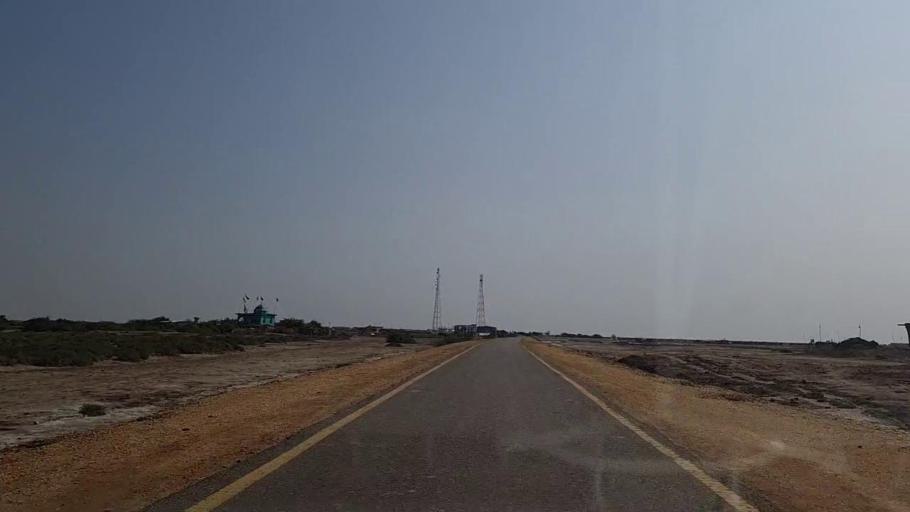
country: PK
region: Sindh
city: Chuhar Jamali
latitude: 24.1681
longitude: 67.8963
